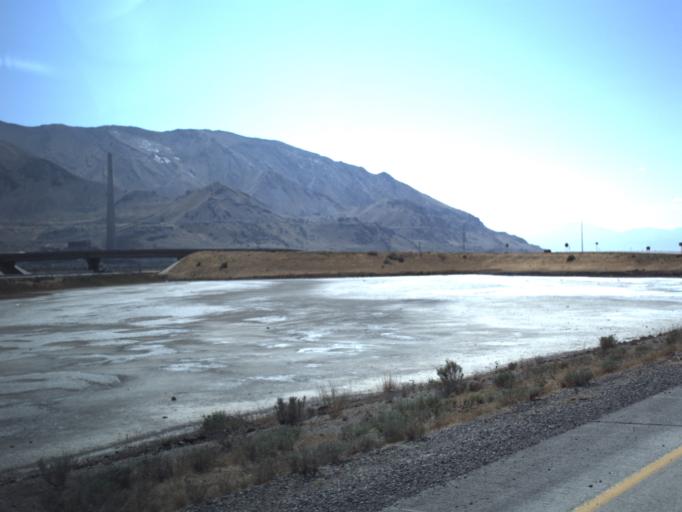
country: US
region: Utah
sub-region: Salt Lake County
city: Magna
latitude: 40.7481
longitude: -112.1814
